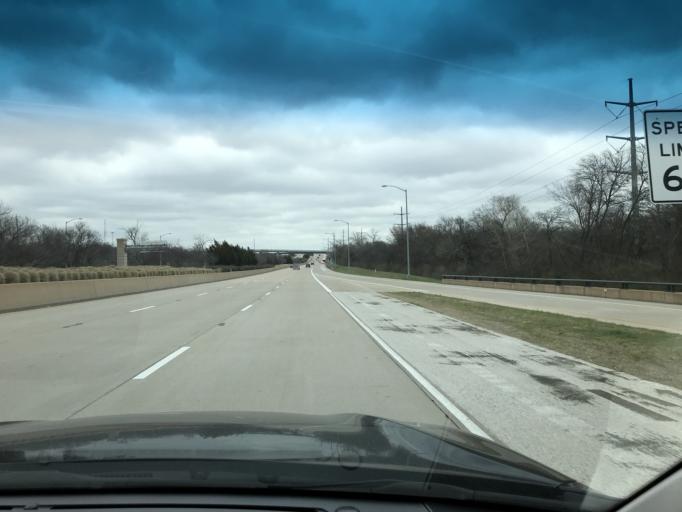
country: US
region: Texas
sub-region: Tarrant County
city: Westworth
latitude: 32.7135
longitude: -97.3962
